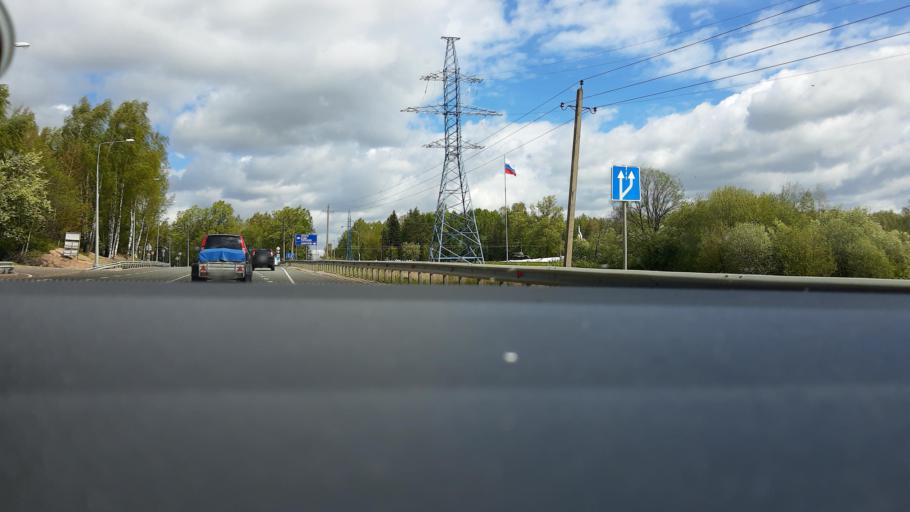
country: RU
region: Moskovskaya
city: Dmitrov
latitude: 56.3561
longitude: 37.4876
